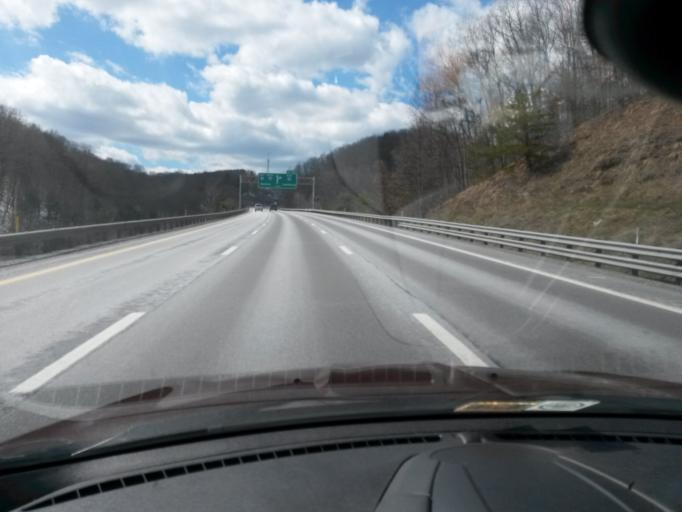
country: US
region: West Virginia
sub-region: Raleigh County
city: Beaver
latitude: 37.7217
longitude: -81.1729
